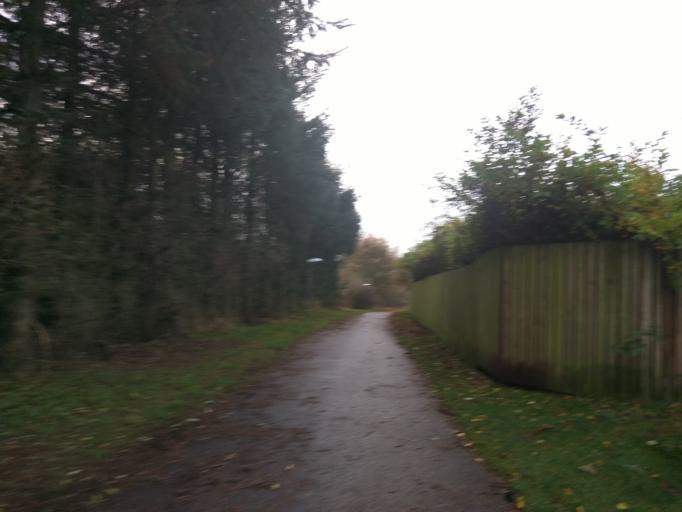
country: DK
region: Central Jutland
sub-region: Viborg Kommune
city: Viborg
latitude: 56.4398
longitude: 9.3840
